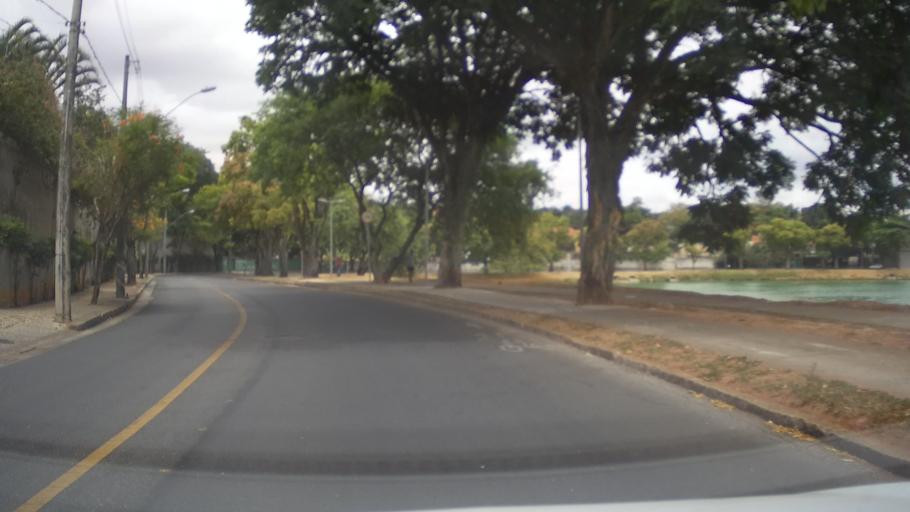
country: BR
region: Minas Gerais
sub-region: Belo Horizonte
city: Belo Horizonte
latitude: -19.8533
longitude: -43.9825
